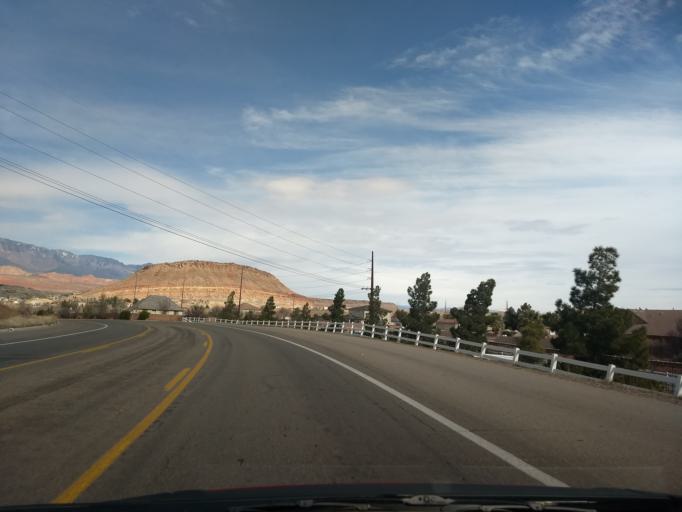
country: US
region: Utah
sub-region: Washington County
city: Washington
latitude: 37.0999
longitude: -113.4964
